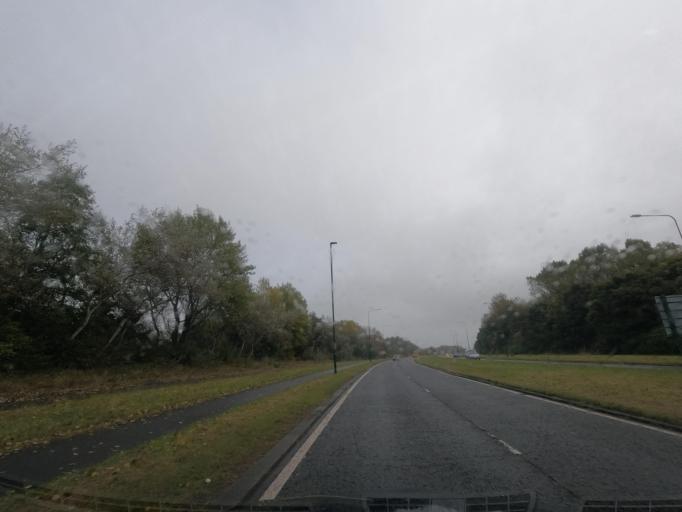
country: GB
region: England
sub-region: Redcar and Cleveland
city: Redcar
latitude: 54.6081
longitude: -1.1075
